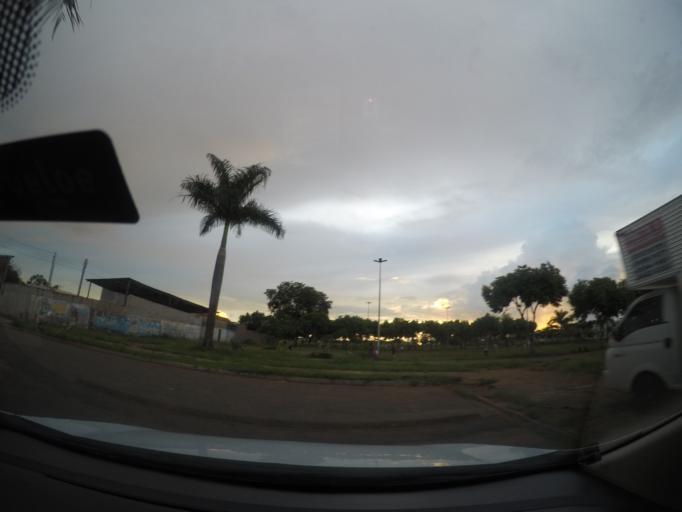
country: BR
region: Goias
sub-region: Goiania
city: Goiania
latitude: -16.7251
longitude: -49.3704
